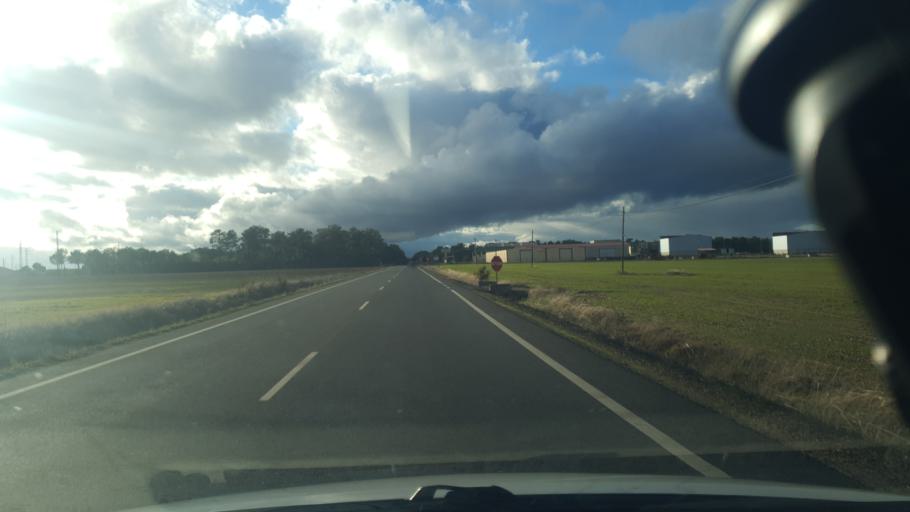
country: ES
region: Castille and Leon
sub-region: Provincia de Segovia
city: Nava de la Asuncion
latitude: 41.1558
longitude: -4.5049
